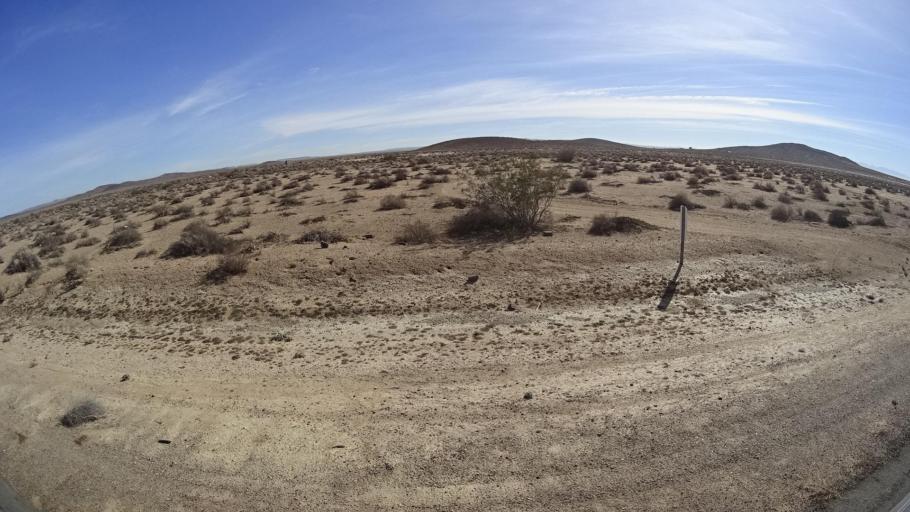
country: US
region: California
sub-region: Kern County
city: North Edwards
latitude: 35.0584
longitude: -117.8090
